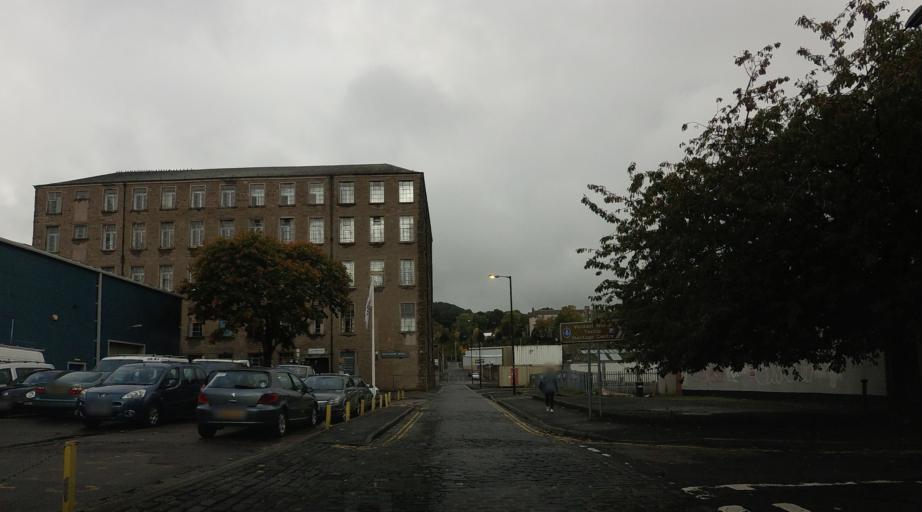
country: GB
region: Scotland
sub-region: Dundee City
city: Dundee
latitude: 56.4619
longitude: -2.9837
